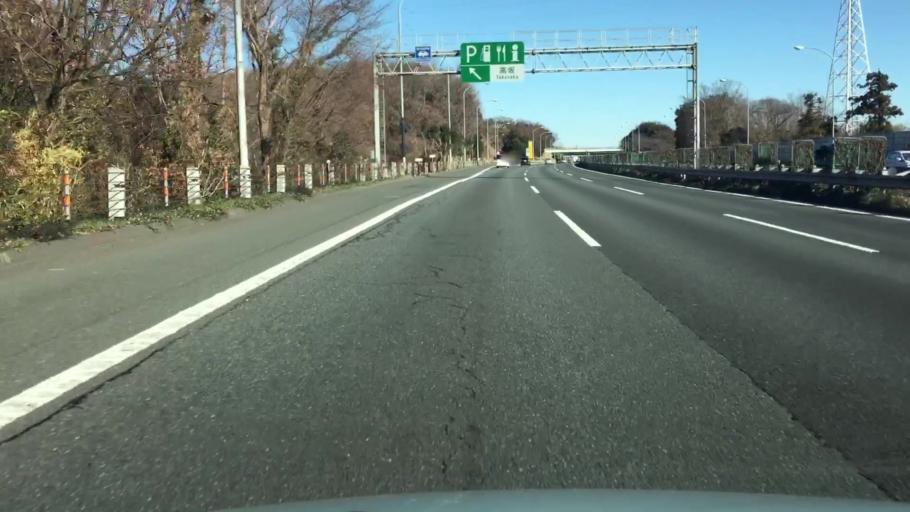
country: JP
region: Saitama
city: Sakado
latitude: 35.9829
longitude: 139.3808
